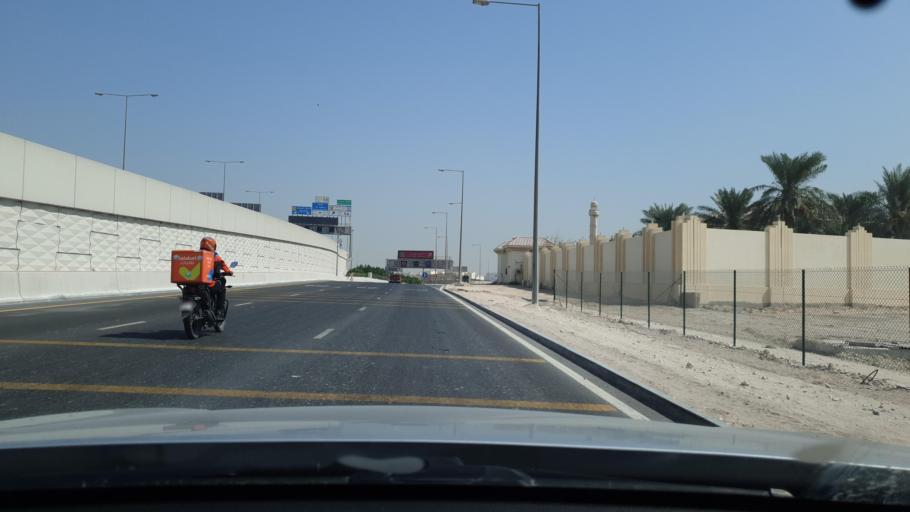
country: QA
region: Baladiyat ad Dawhah
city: Doha
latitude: 25.2352
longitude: 51.5206
